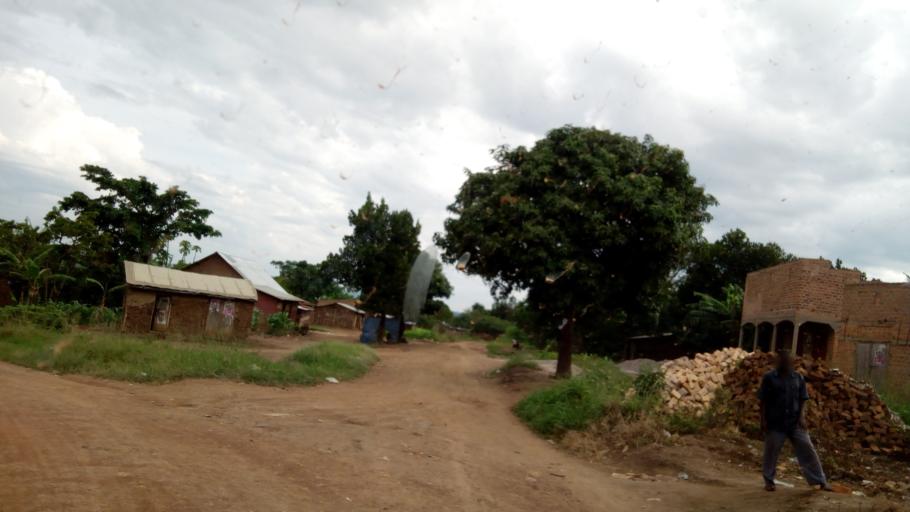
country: UG
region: Central Region
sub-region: Kiboga District
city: Kiboga
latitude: 0.7492
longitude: 31.7434
